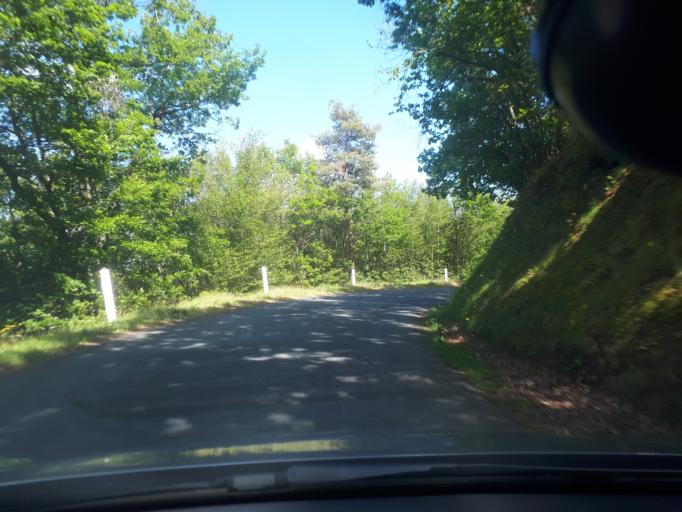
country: FR
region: Rhone-Alpes
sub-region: Departement du Rhone
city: Thurins
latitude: 45.6440
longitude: 4.6102
